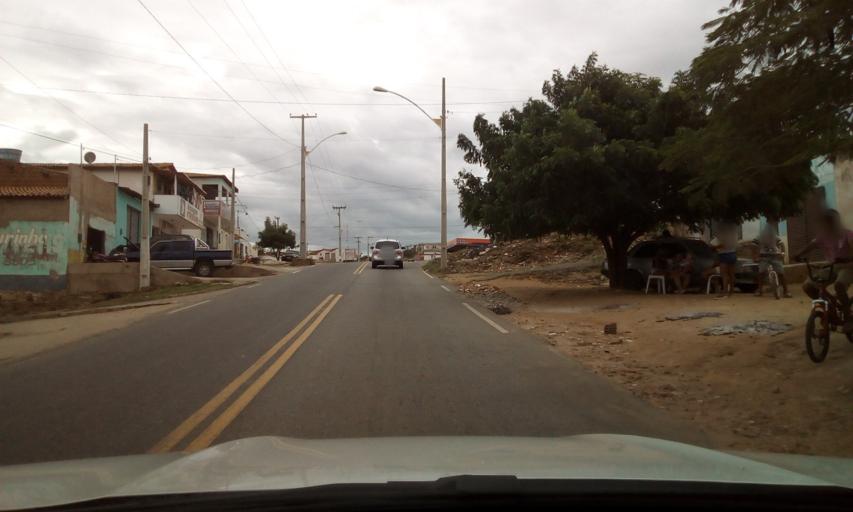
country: BR
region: Paraiba
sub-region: Picui
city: Picui
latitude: -6.5122
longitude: -36.3377
